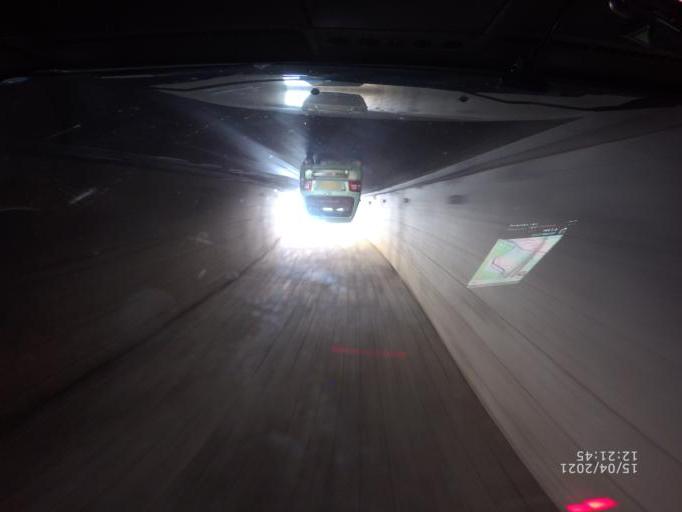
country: IR
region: Tehran
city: Shahrak-e Emam Hasan-e Mojtaba
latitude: 35.5109
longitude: 51.2962
